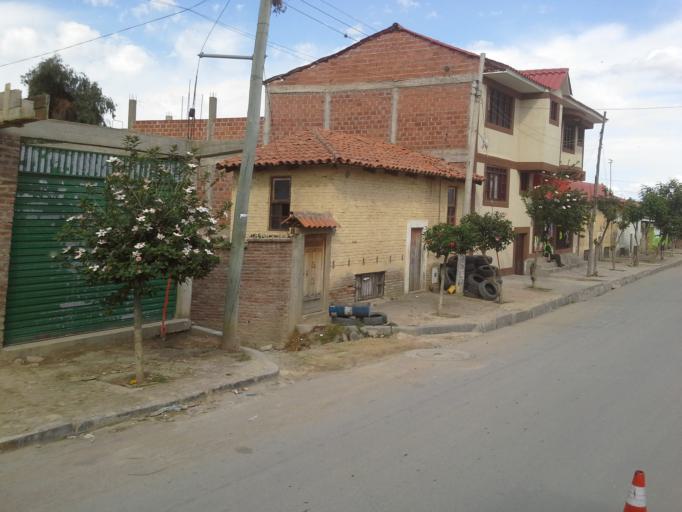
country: BO
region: Cochabamba
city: Tarata
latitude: -17.6104
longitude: -66.0221
